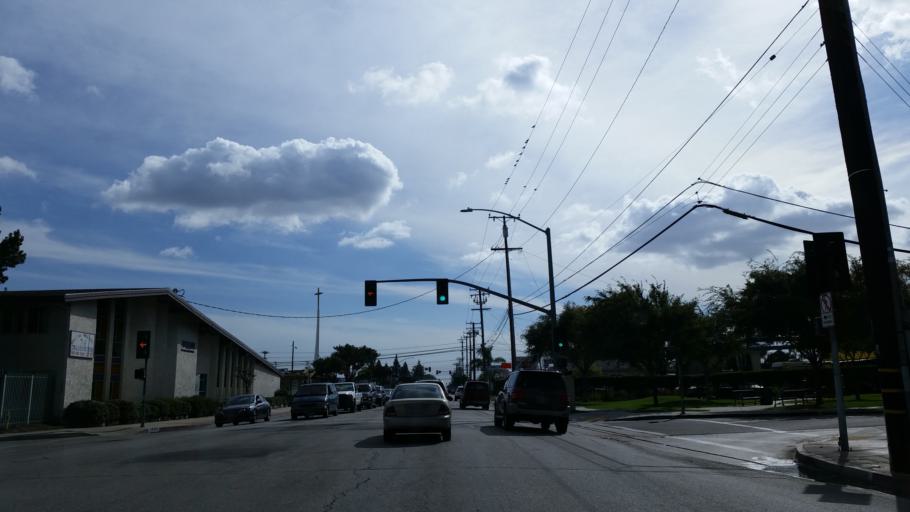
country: US
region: California
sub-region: Los Angeles County
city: Bellflower
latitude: 33.8770
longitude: -118.1339
